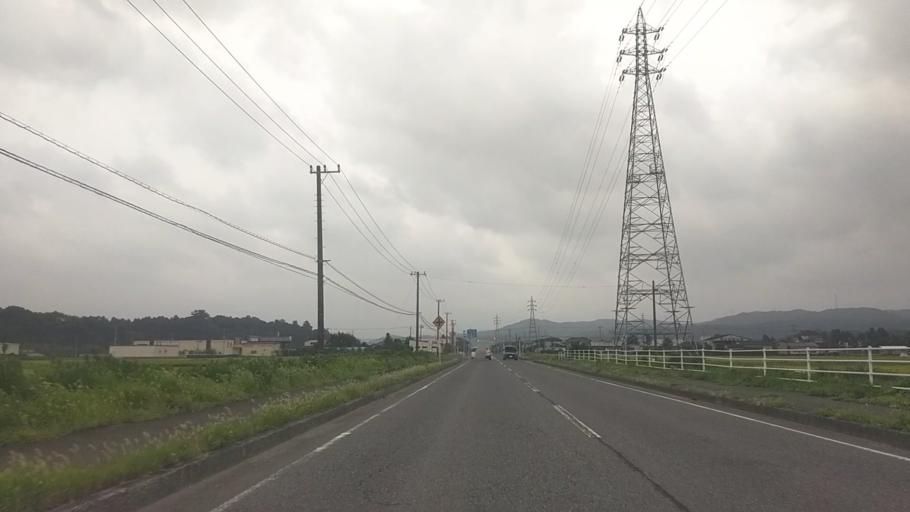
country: JP
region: Chiba
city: Kisarazu
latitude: 35.3276
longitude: 140.0550
